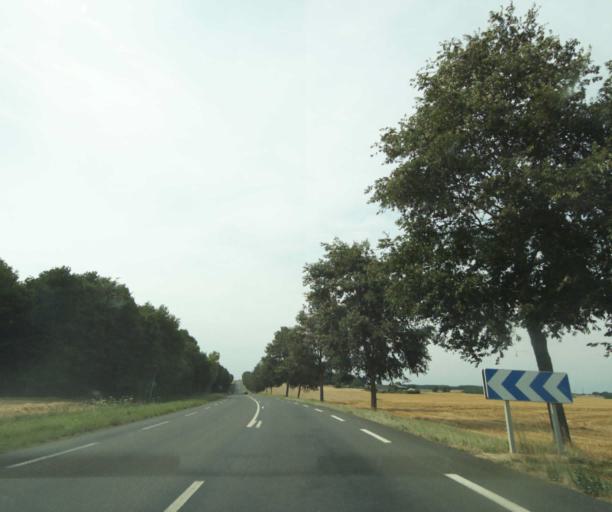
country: FR
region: Centre
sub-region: Departement d'Indre-et-Loire
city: Saint-Christophe-sur-le-Nais
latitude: 47.6464
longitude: 0.4967
